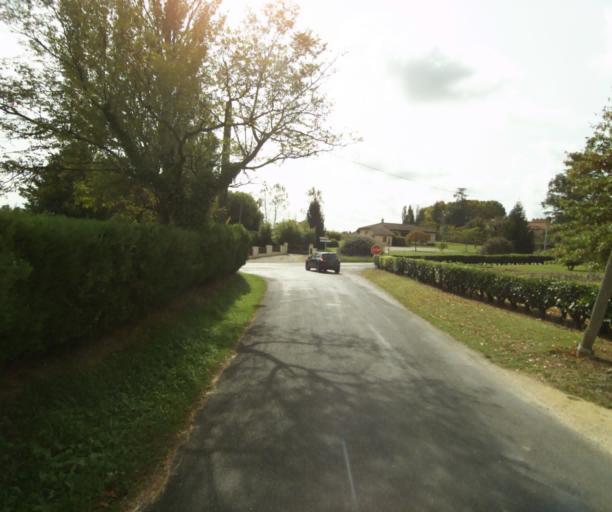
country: FR
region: Midi-Pyrenees
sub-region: Departement du Gers
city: Eauze
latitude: 43.8582
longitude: 0.0814
